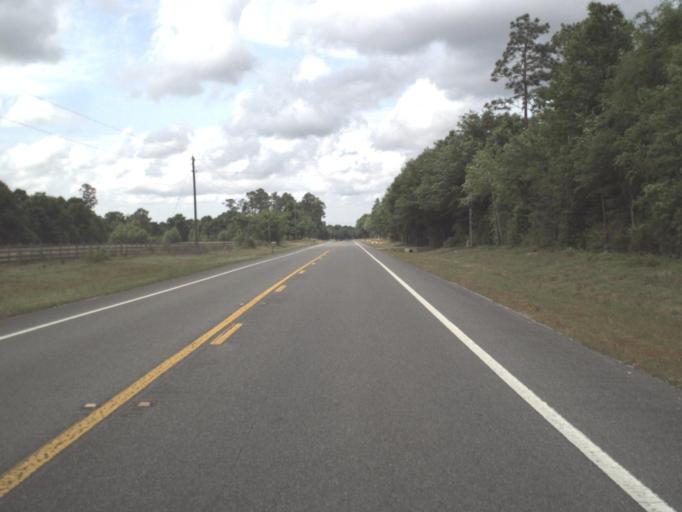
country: US
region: Florida
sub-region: Santa Rosa County
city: Point Baker
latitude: 30.7266
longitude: -87.0817
